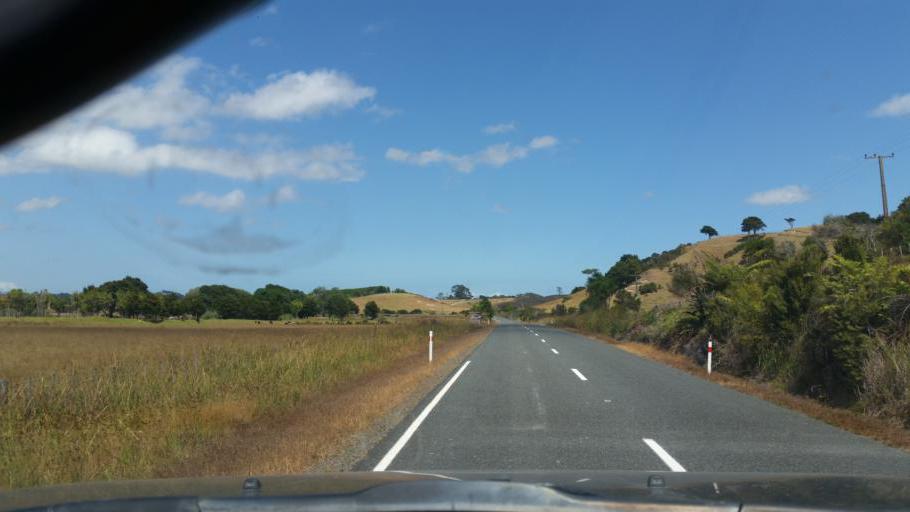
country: NZ
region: Northland
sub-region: Kaipara District
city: Dargaville
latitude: -35.8946
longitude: 173.8415
